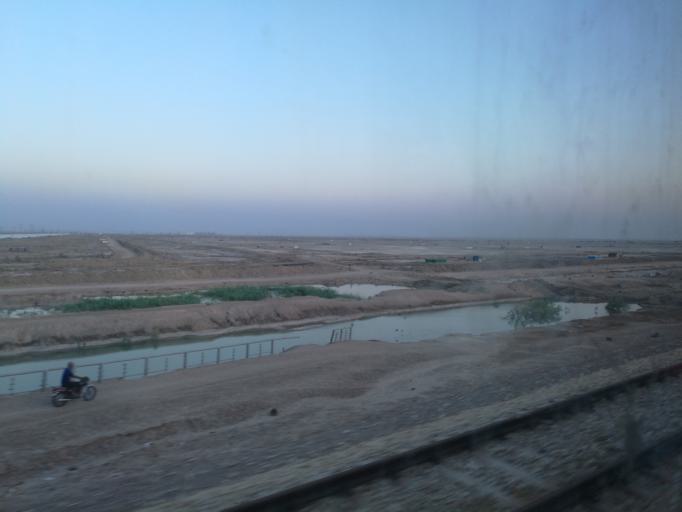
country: IQ
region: Basra Governorate
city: Al Harithah
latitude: 30.5191
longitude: 47.7201
